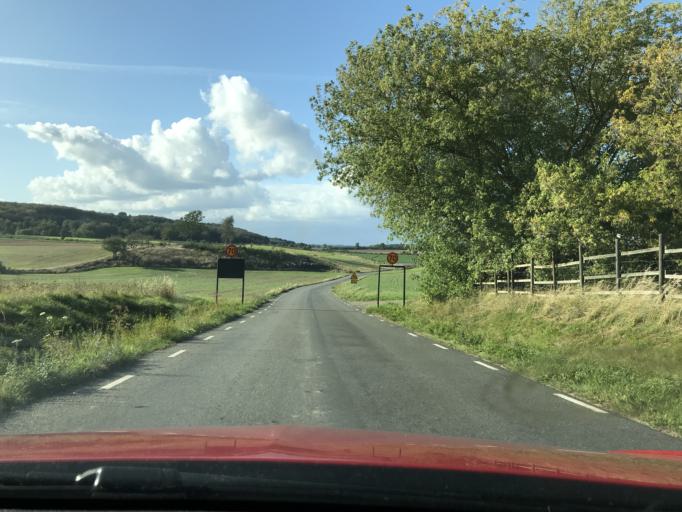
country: SE
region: Skane
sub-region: Kristianstads Kommun
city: Degeberga
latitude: 55.8417
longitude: 14.0869
